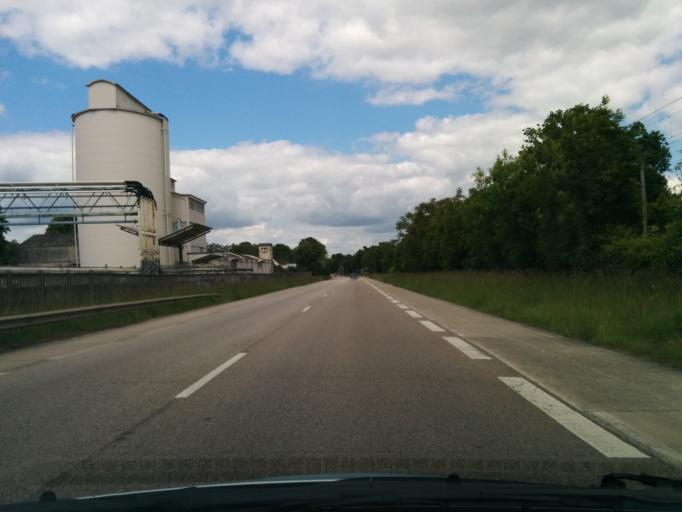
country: FR
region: Ile-de-France
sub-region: Departement des Yvelines
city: Mantes-la-Jolie
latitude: 48.9736
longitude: 1.7360
